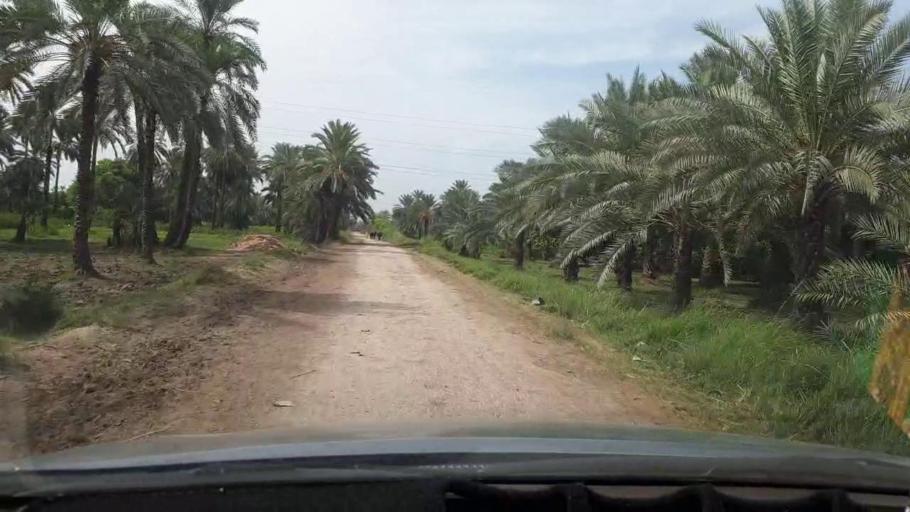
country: PK
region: Sindh
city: Khairpur
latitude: 27.5025
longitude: 68.7555
